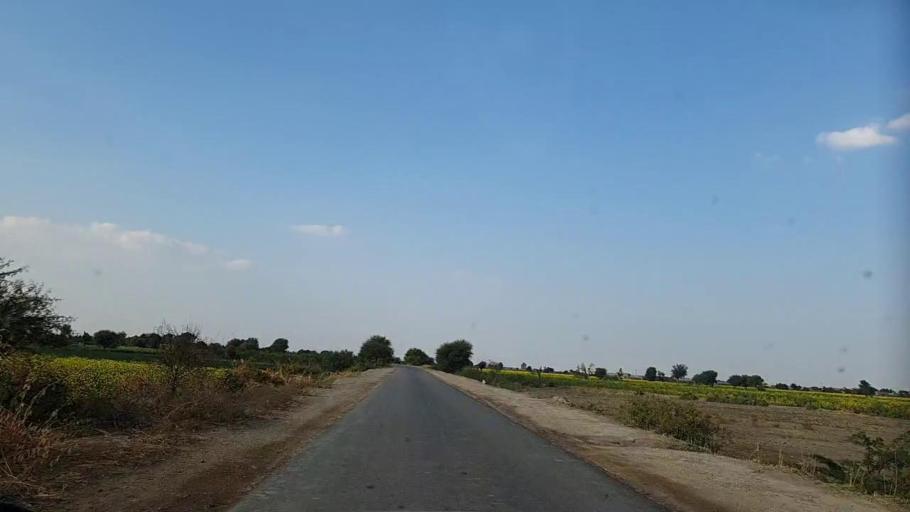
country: PK
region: Sindh
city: Pithoro
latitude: 25.6828
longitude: 69.2258
